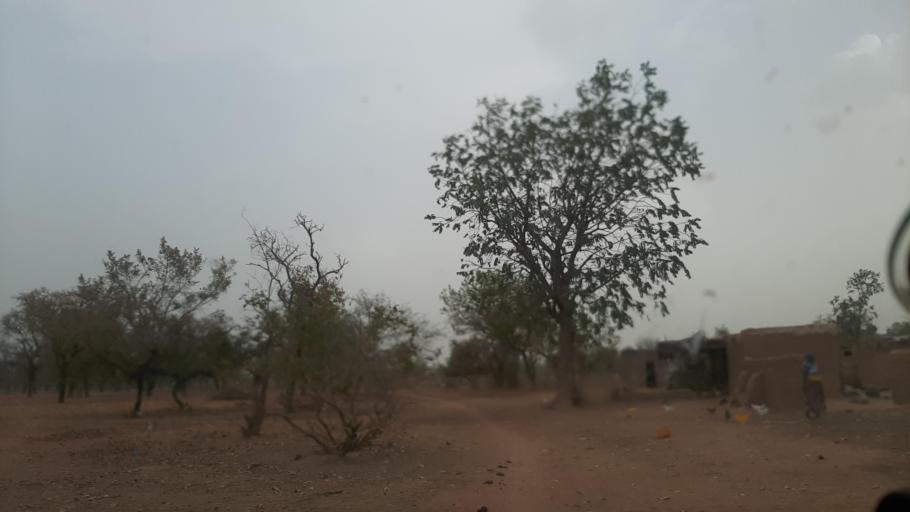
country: BF
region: Boucle du Mouhoun
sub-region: Province des Banwa
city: Salanso
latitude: 11.8685
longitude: -4.4458
